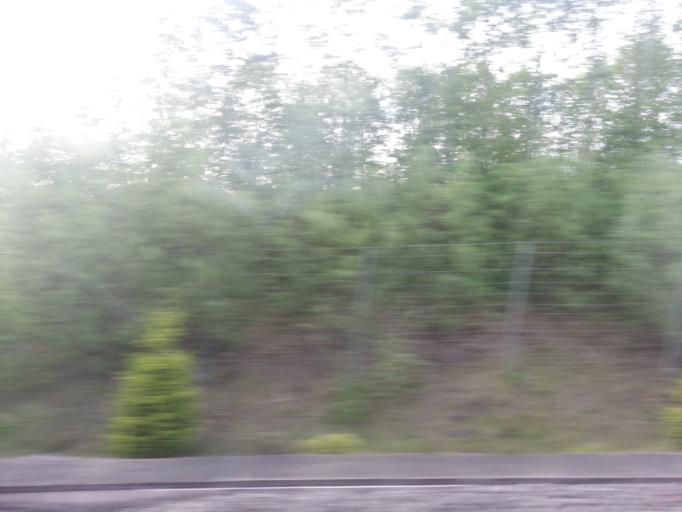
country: NO
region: Akershus
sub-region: Sorum
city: Frogner
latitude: 60.0385
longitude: 11.1282
